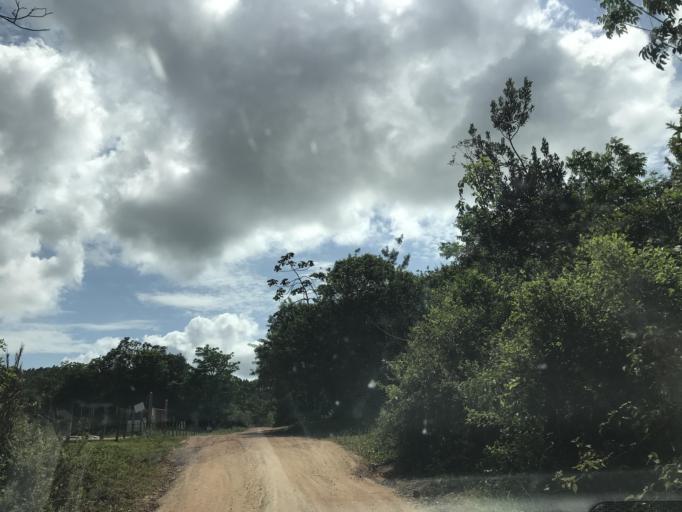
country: BR
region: Bahia
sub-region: Entre Rios
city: Entre Rios
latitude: -12.1688
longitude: -38.0682
